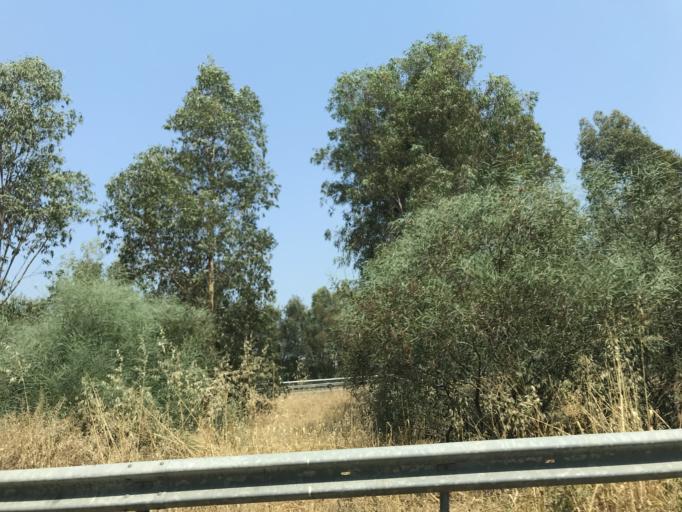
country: TR
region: Aydin
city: Ortaklar
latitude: 37.8342
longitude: 27.5282
